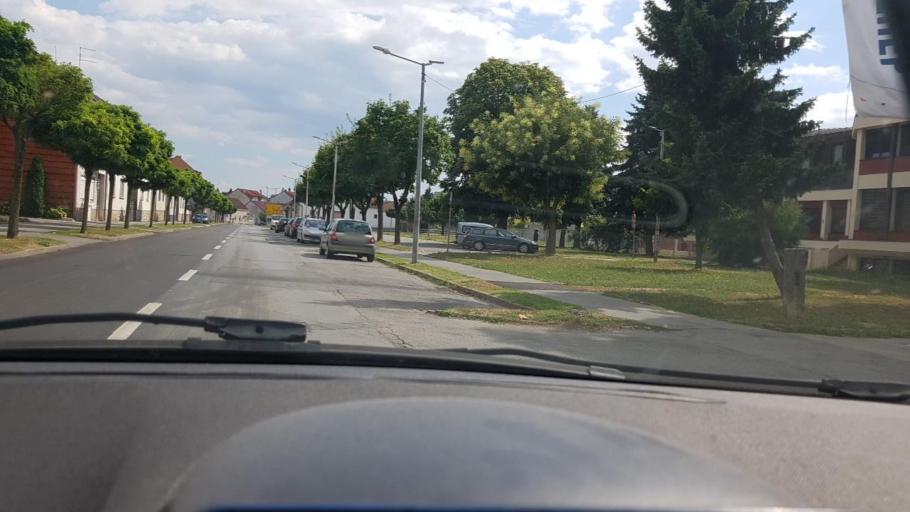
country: HR
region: Bjelovarsko-Bilogorska
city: Bjelovar
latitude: 45.9068
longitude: 16.8468
